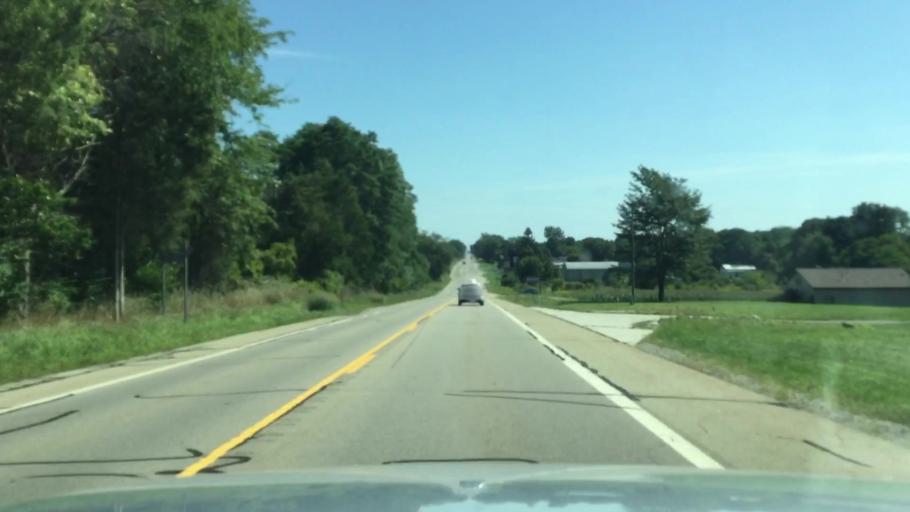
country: US
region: Michigan
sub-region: Washtenaw County
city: Manchester
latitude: 42.0725
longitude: -84.0724
